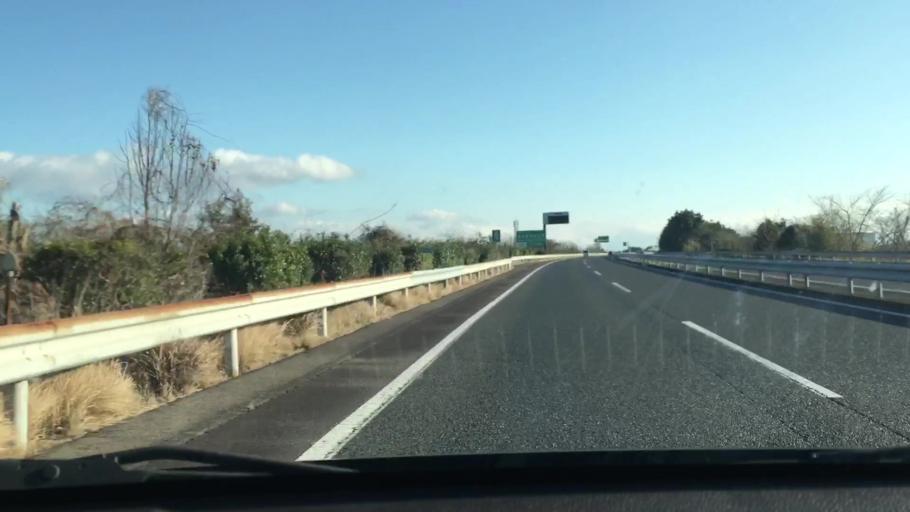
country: JP
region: Kagoshima
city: Kajiki
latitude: 31.7959
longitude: 130.7156
